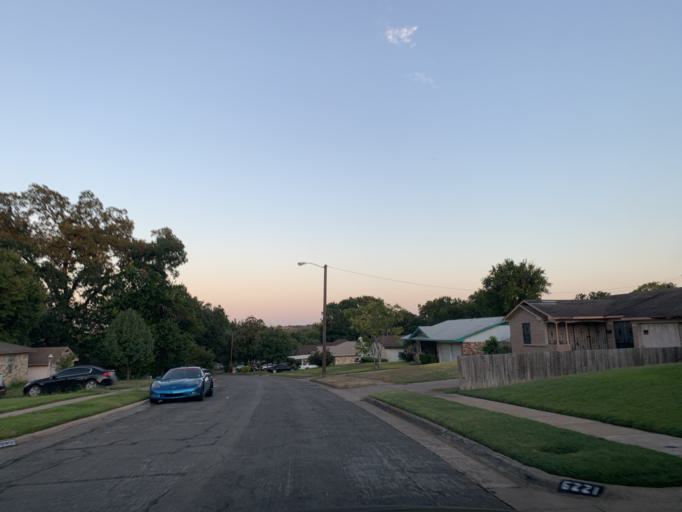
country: US
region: Texas
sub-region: Dallas County
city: Hutchins
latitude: 32.6724
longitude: -96.7991
